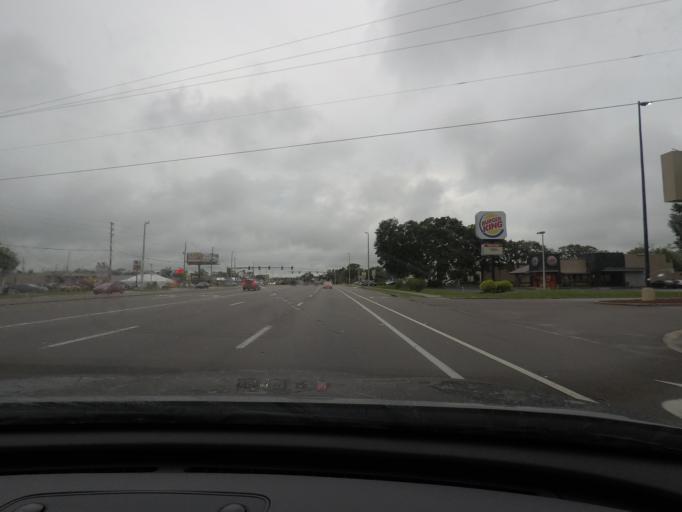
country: US
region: Florida
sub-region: Orange County
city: Union Park
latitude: 28.5685
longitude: -81.2845
